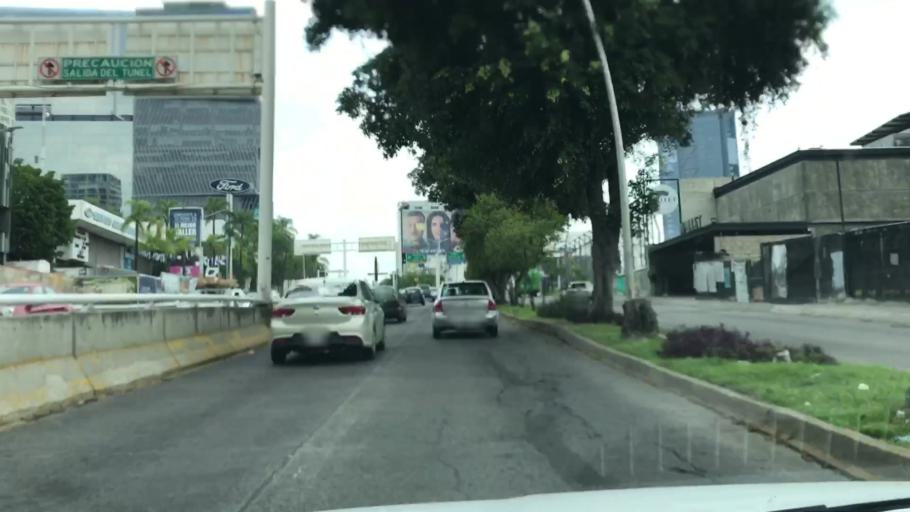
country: MX
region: Jalisco
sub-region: Zapopan
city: Zapopan
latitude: 20.7008
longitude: -103.3754
